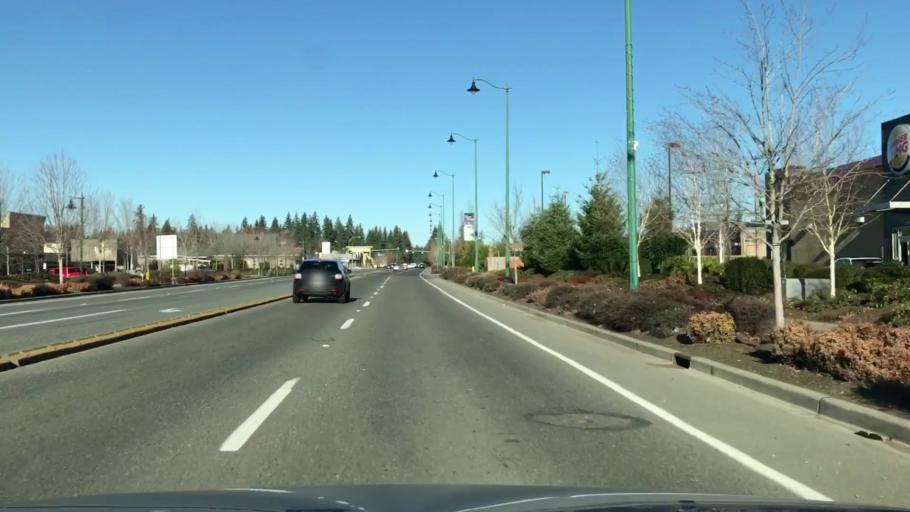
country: US
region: Washington
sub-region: King County
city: Ravensdale
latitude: 47.3626
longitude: -122.0211
